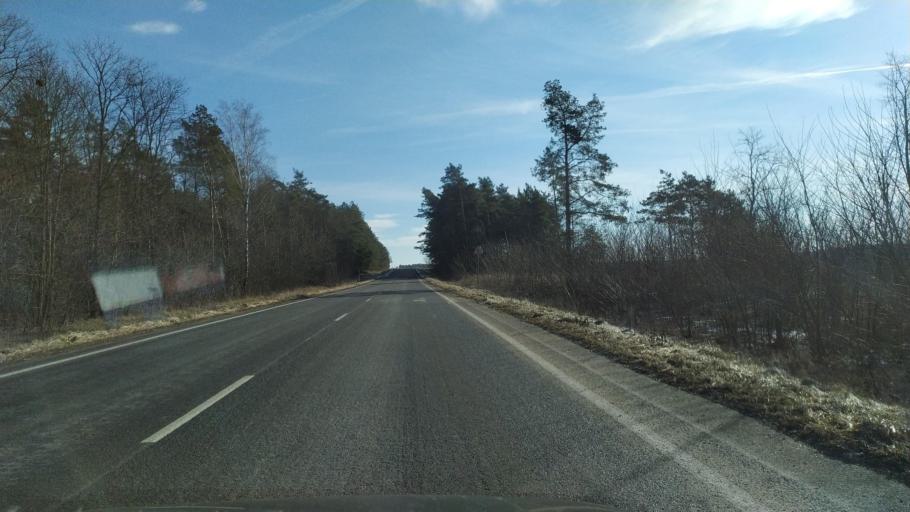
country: BY
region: Brest
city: Kamyanyets
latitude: 52.3992
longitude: 23.9055
